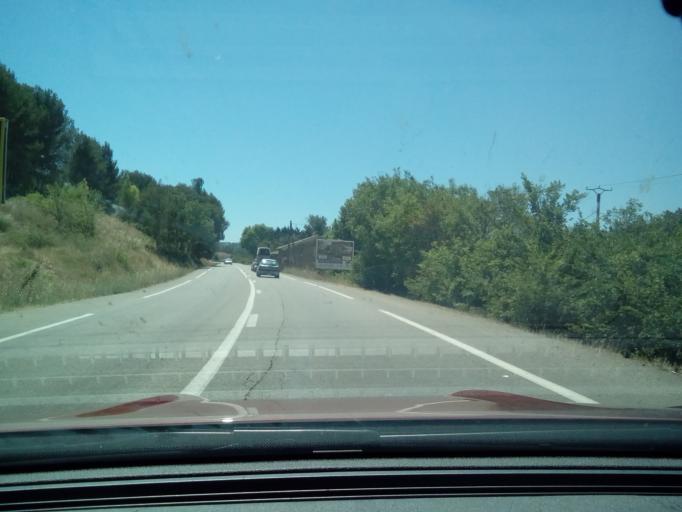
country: FR
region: Provence-Alpes-Cote d'Azur
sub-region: Departement des Bouches-du-Rhone
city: Meyreuil
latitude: 43.4908
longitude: 5.5249
